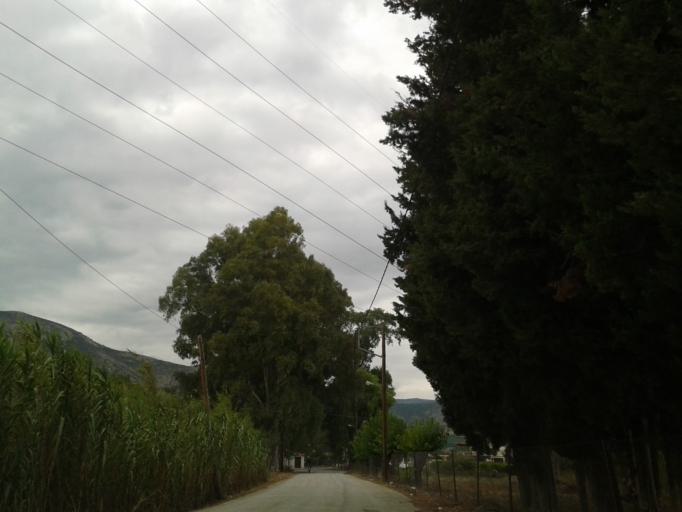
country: GR
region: Peloponnese
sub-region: Nomos Argolidos
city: Nea Kios
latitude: 37.5967
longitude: 22.7037
